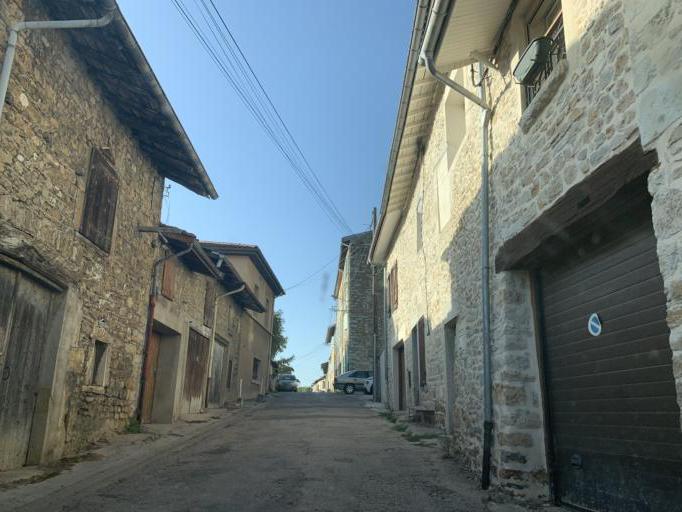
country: FR
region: Rhone-Alpes
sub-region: Departement de l'Ain
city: Vaux-en-Bugey
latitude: 45.9471
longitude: 5.3724
